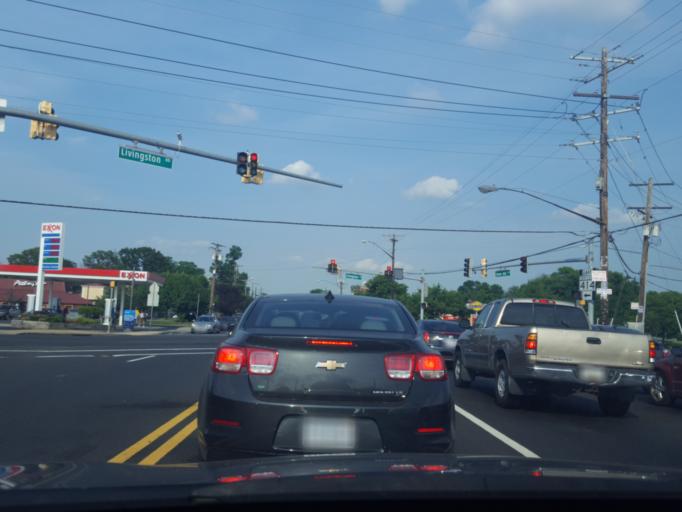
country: US
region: Maryland
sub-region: Prince George's County
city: Oxon Hill
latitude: 38.8033
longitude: -76.9902
